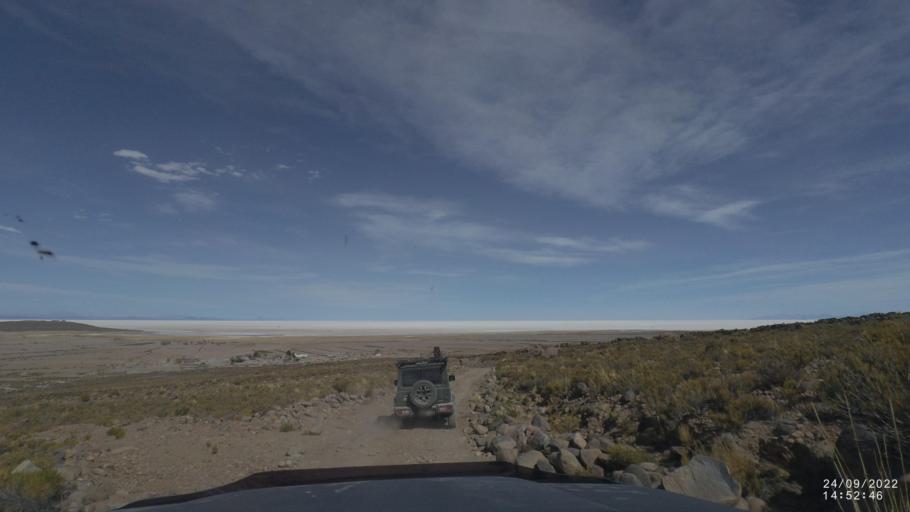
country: BO
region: Potosi
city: Colchani
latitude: -19.8536
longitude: -67.5796
